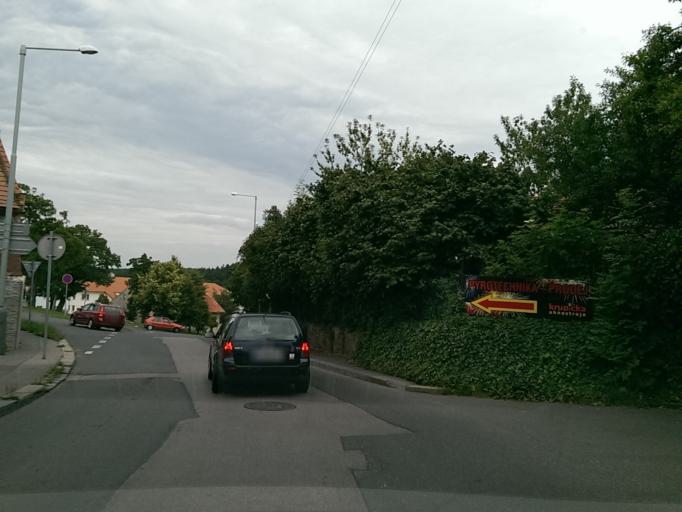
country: CZ
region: Praha
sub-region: Praha 14
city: Dolni Pocernice
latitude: 50.0636
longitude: 14.5934
